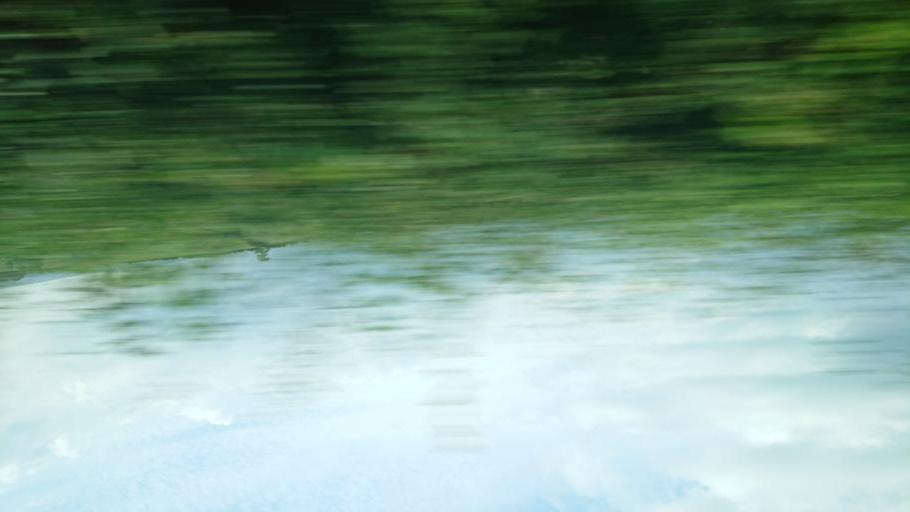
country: GB
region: England
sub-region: North Yorkshire
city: Ingleton
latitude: 54.1458
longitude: -2.4943
